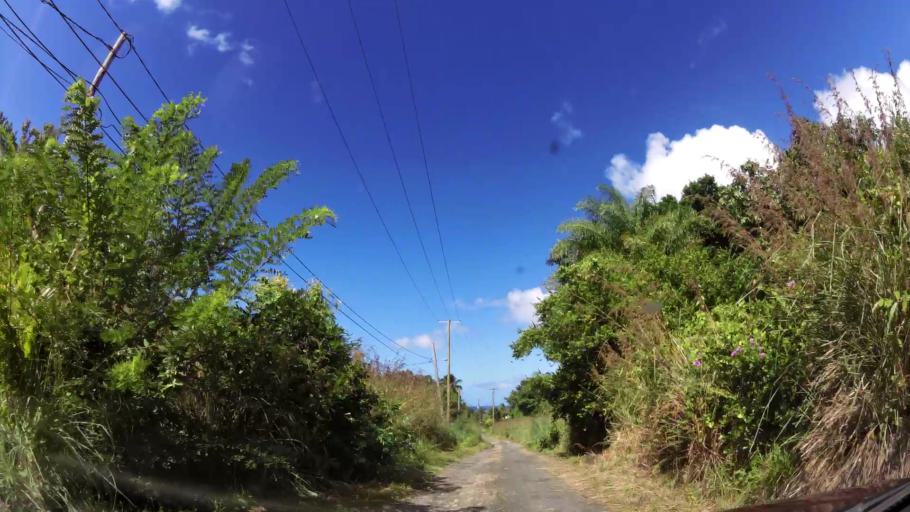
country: DM
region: Saint John
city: Portsmouth
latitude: 15.5601
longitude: -61.4511
